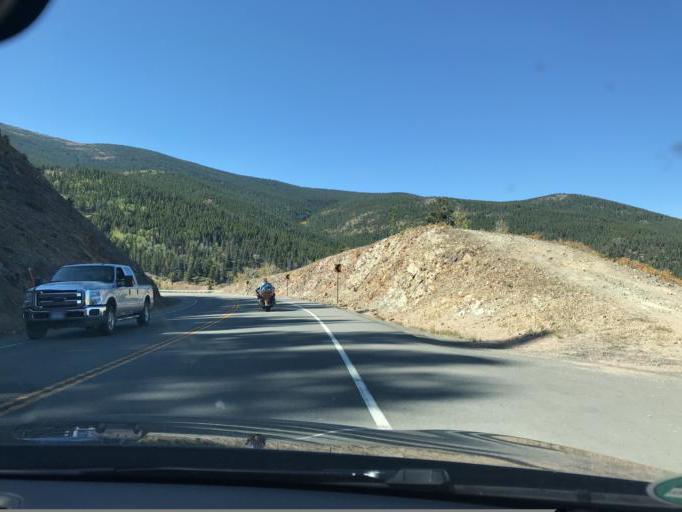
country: US
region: Colorado
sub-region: Boulder County
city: Nederland
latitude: 40.0529
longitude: -105.5197
